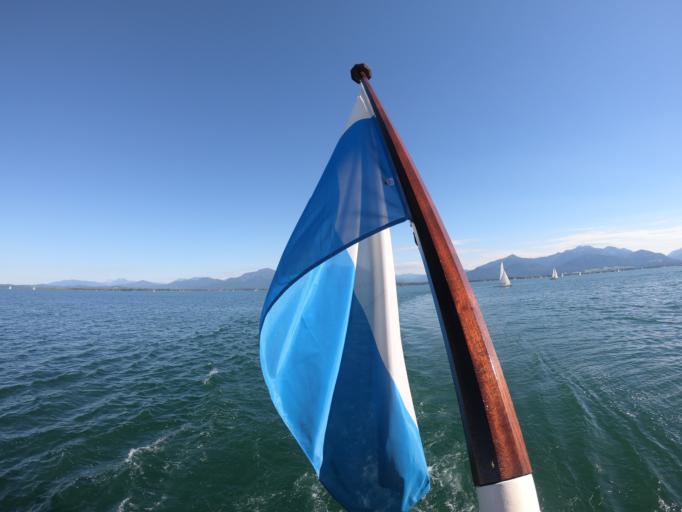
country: DE
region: Bavaria
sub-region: Upper Bavaria
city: Chiemsee
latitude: 47.8704
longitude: 12.4288
